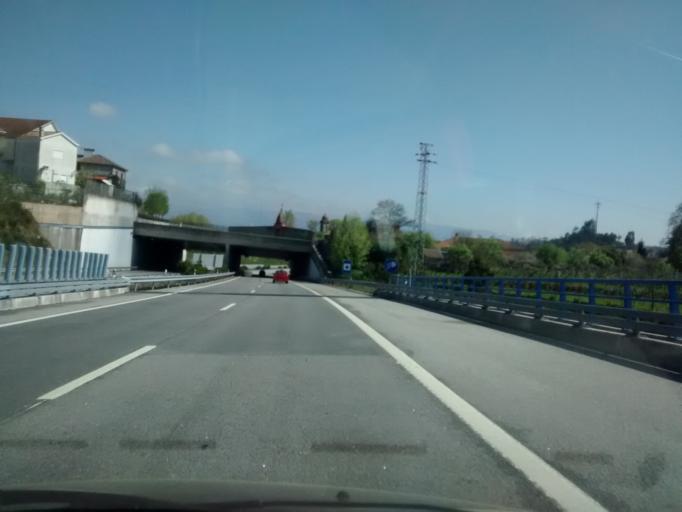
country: PT
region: Braga
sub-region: Cabeceiras de Basto
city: Refojos de Basto
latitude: 41.4570
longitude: -8.0333
